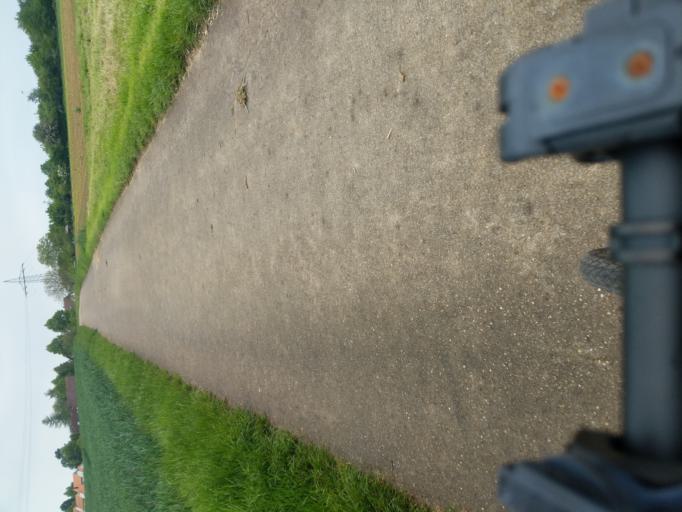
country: DE
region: Baden-Wuerttemberg
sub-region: Regierungsbezirk Stuttgart
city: Waiblingen
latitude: 48.8584
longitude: 9.2893
